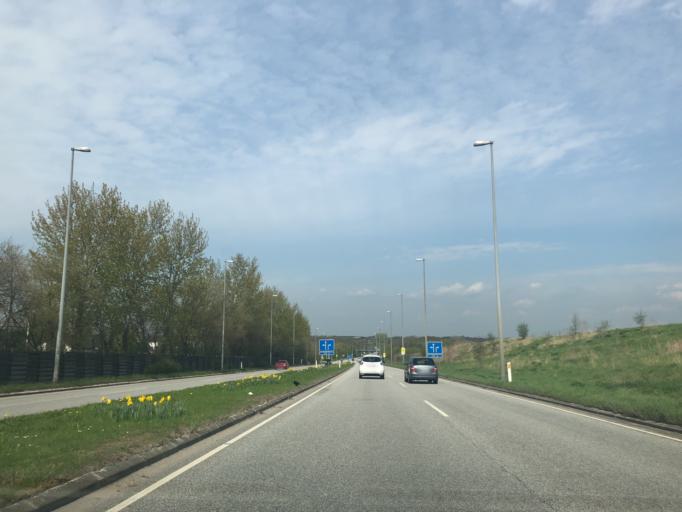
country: DK
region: Zealand
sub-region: Roskilde Kommune
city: Vindinge
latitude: 55.6483
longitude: 12.1183
